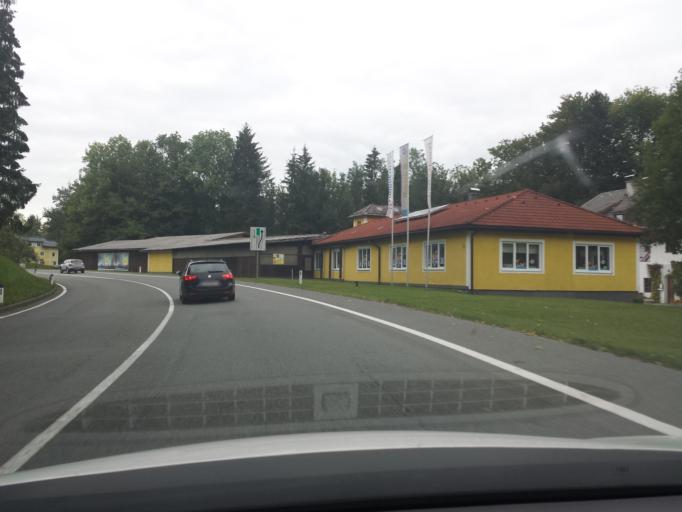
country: AT
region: Salzburg
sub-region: Politischer Bezirk Salzburg-Umgebung
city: Plainfeld
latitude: 47.8145
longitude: 13.1770
